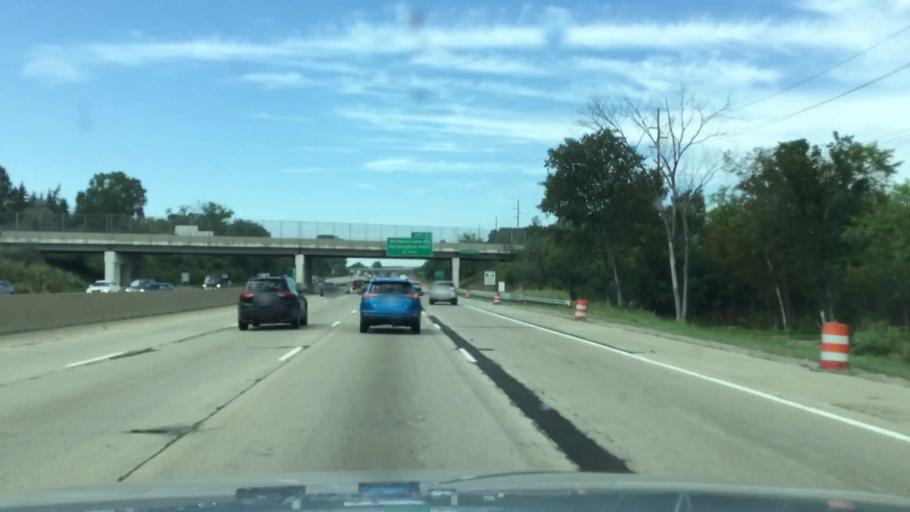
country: US
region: Michigan
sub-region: Oakland County
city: Farmington Hills
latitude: 42.4926
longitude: -83.3373
